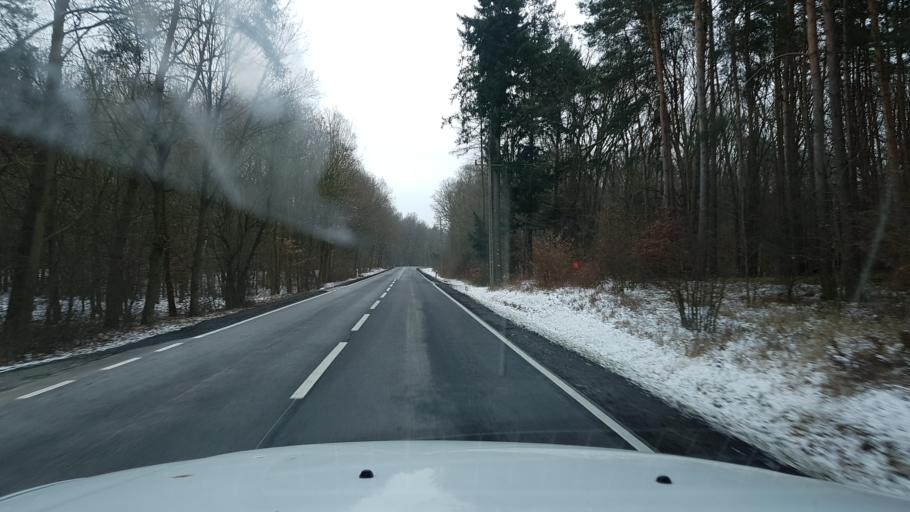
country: PL
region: West Pomeranian Voivodeship
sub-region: Powiat gryfinski
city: Widuchowa
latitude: 53.1118
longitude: 14.4058
